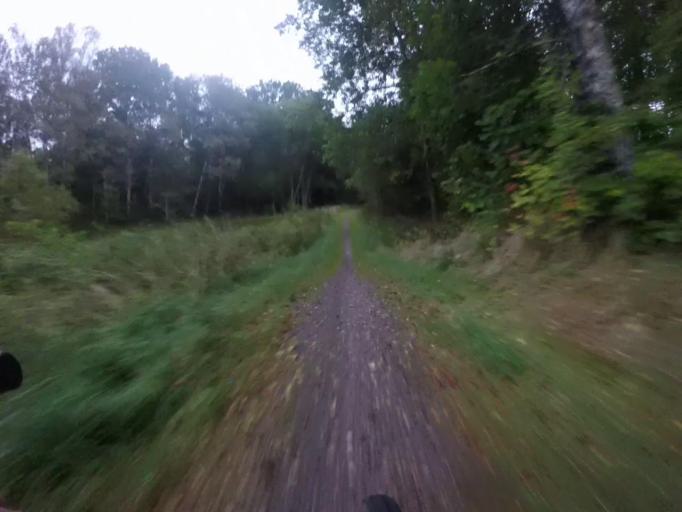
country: SE
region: Vaestra Goetaland
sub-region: Trollhattan
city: Trollhattan
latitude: 58.2816
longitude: 12.2623
